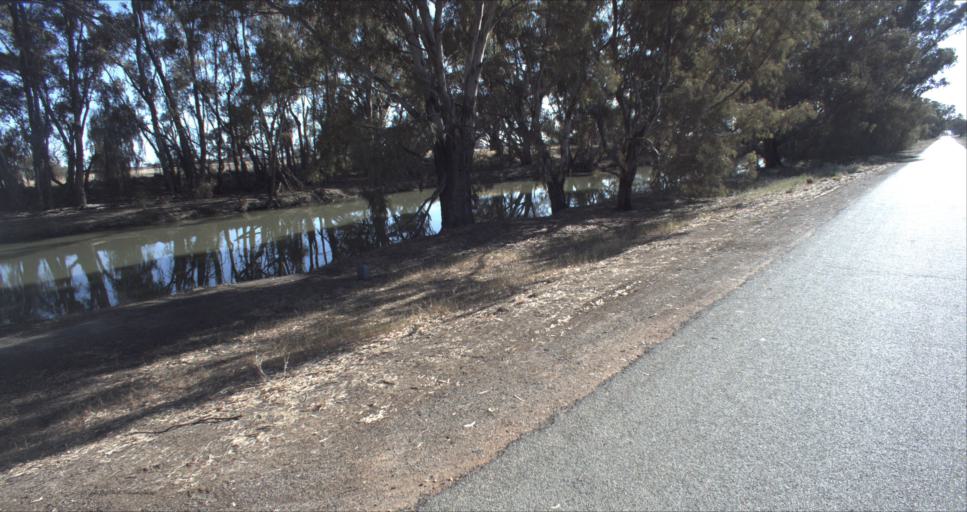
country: AU
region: New South Wales
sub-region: Leeton
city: Leeton
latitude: -34.6061
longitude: 146.2578
